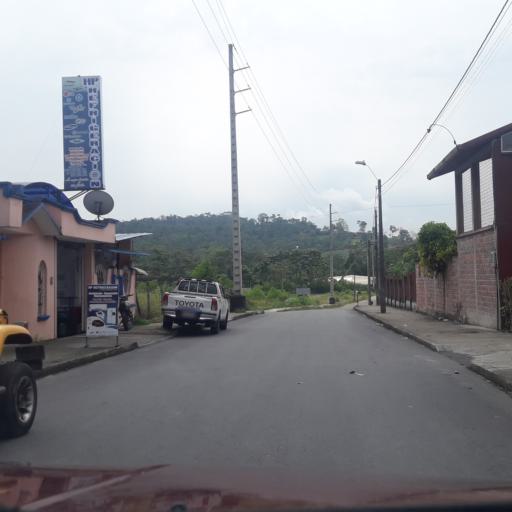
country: EC
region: Napo
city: Tena
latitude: -0.9826
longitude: -77.8122
